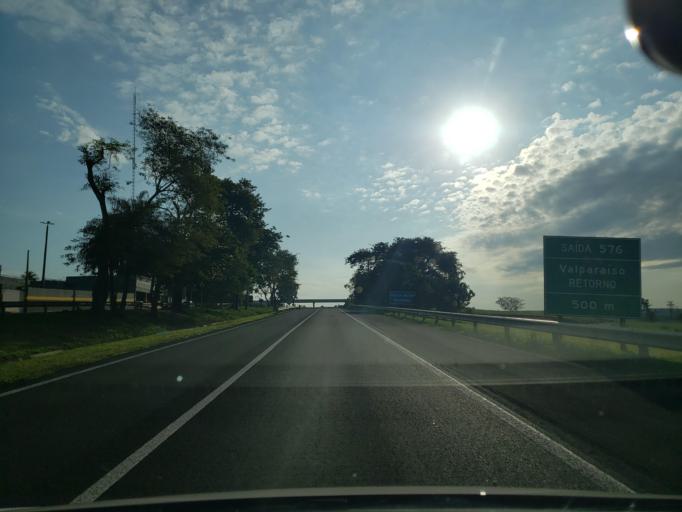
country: BR
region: Sao Paulo
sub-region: Valparaiso
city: Valparaiso
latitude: -21.2134
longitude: -50.8627
